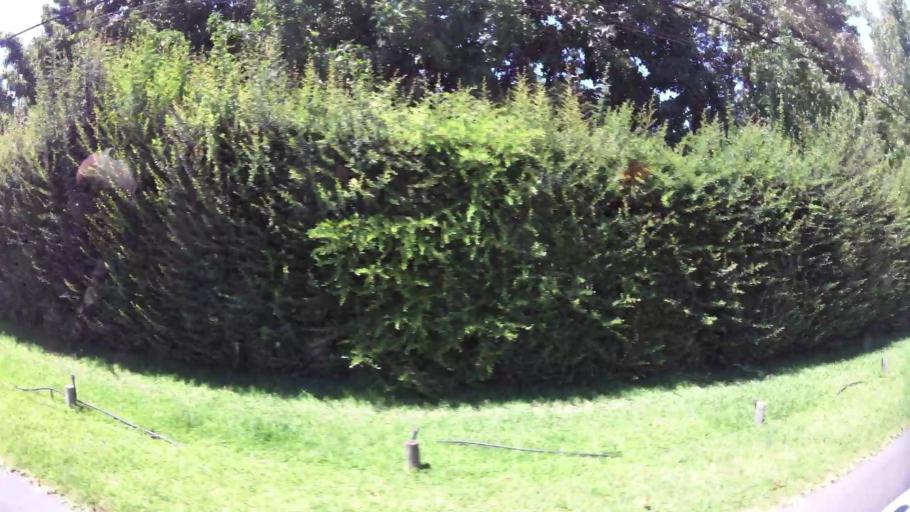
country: CL
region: Maule
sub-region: Provincia de Curico
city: Curico
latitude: -34.9945
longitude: -71.2106
